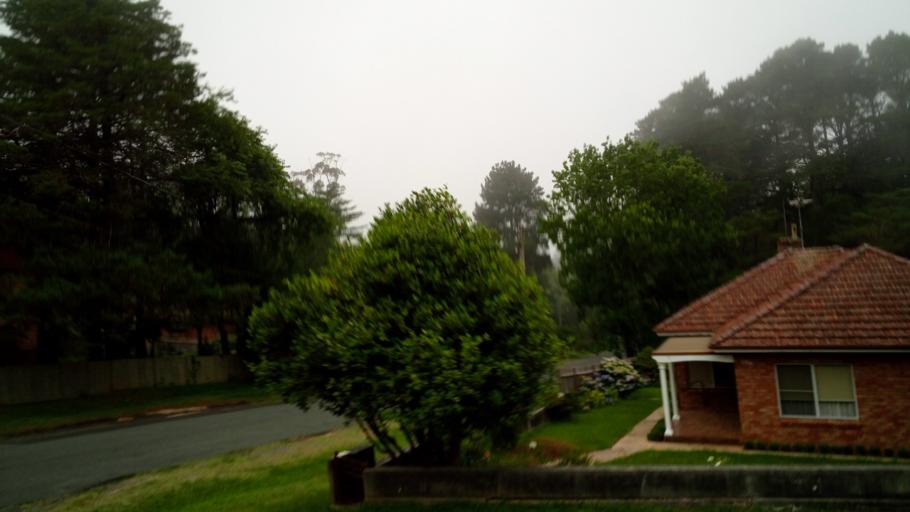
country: AU
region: New South Wales
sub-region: Blue Mountains Municipality
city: Leura
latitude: -33.7228
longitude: 150.3285
